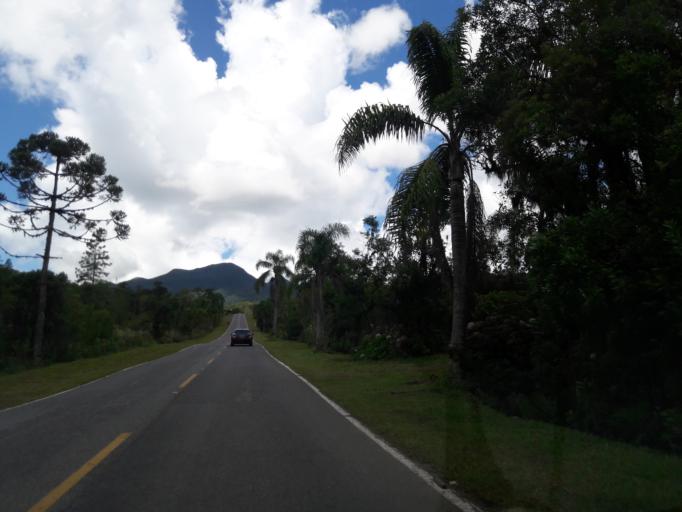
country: BR
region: Parana
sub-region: Campina Grande Do Sul
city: Campina Grande do Sul
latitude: -25.3176
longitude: -48.9286
